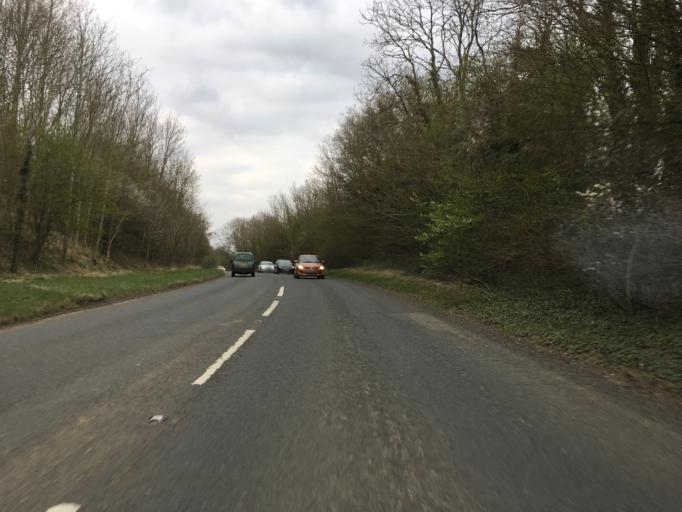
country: GB
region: England
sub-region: Gloucestershire
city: Cirencester
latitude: 51.7308
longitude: -1.9101
